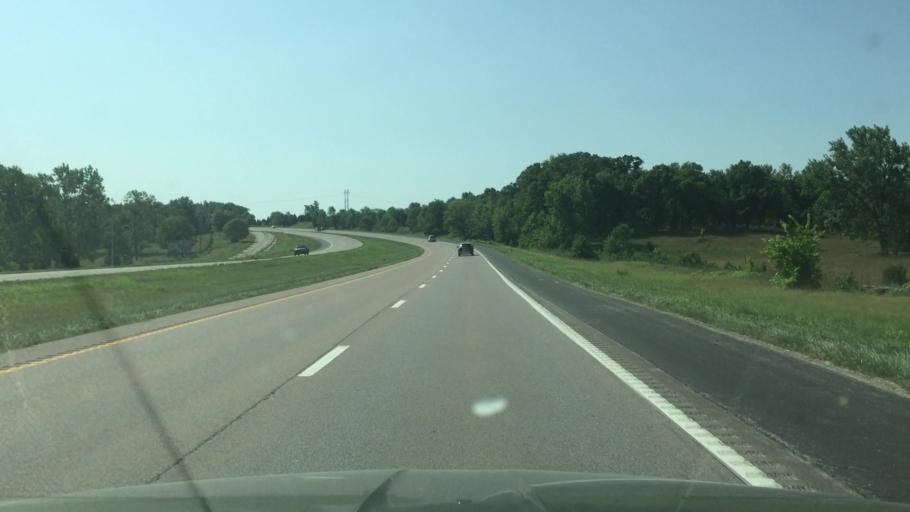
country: US
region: Missouri
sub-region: Pettis County
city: Sedalia
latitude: 38.7236
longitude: -93.3017
